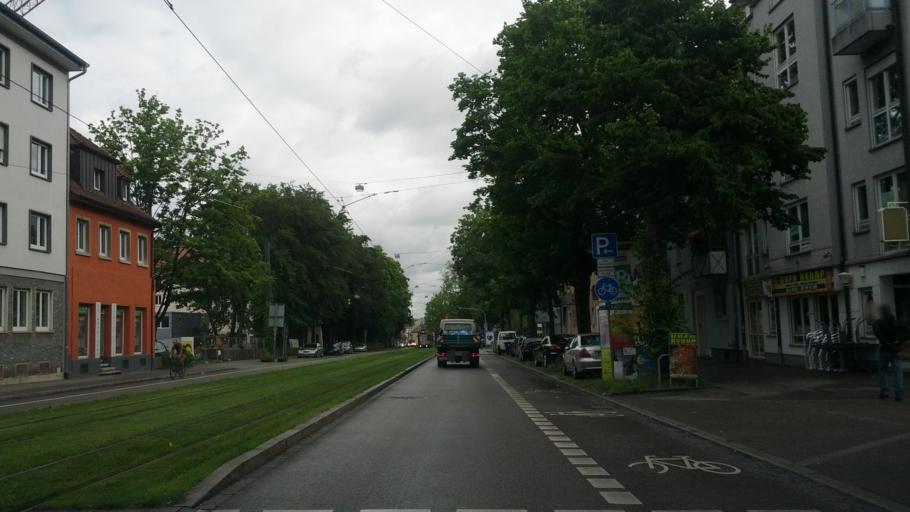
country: DE
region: Baden-Wuerttemberg
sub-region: Freiburg Region
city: Freiburg
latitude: 47.9998
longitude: 7.8537
